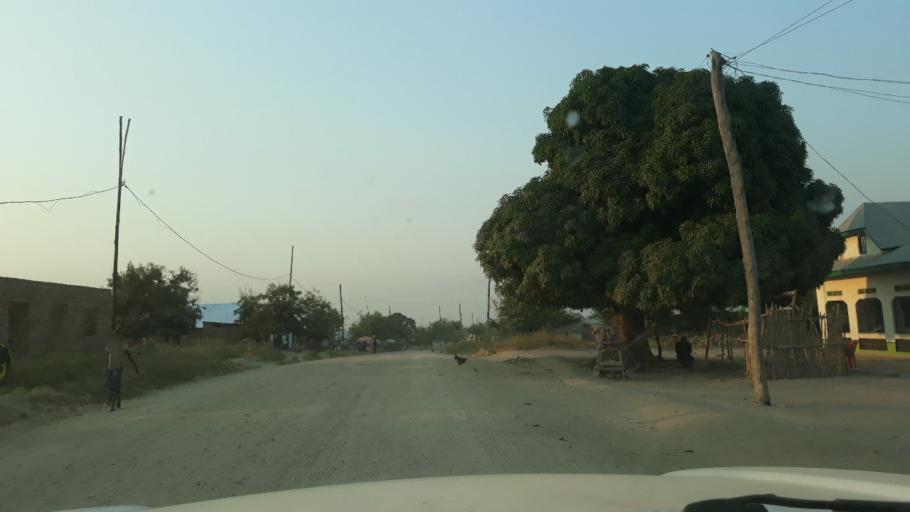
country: BI
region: Bururi
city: Rumonge
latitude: -4.1148
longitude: 29.0873
